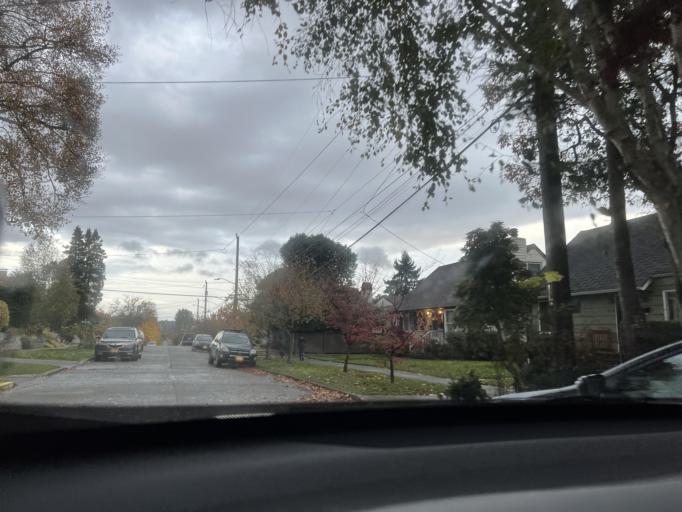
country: US
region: Washington
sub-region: King County
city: Seattle
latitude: 47.6752
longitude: -122.3966
